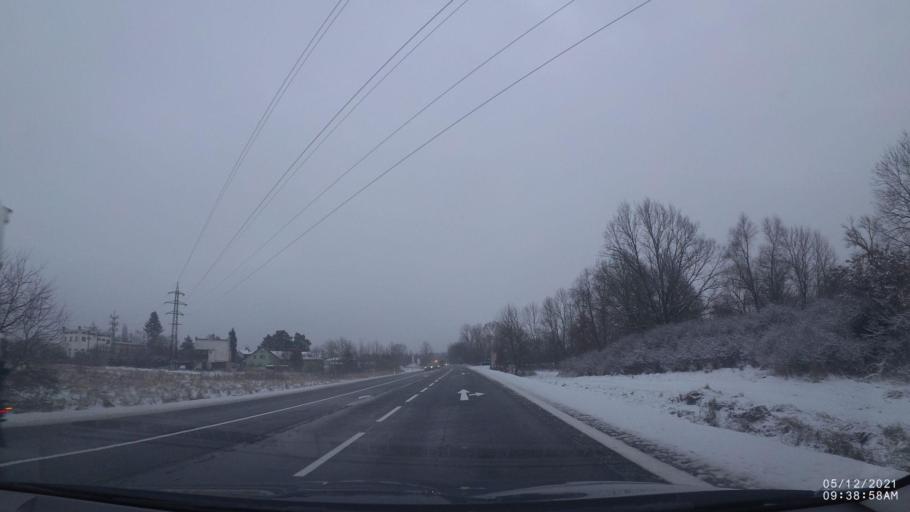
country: CZ
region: Kralovehradecky
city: Trebechovice pod Orebem
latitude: 50.1962
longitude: 15.9850
